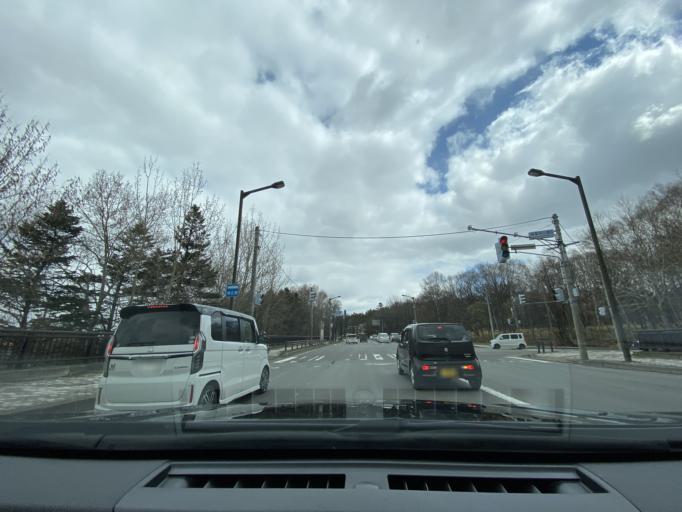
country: JP
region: Hokkaido
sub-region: Asahikawa-shi
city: Asahikawa
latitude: 43.7505
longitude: 142.3607
